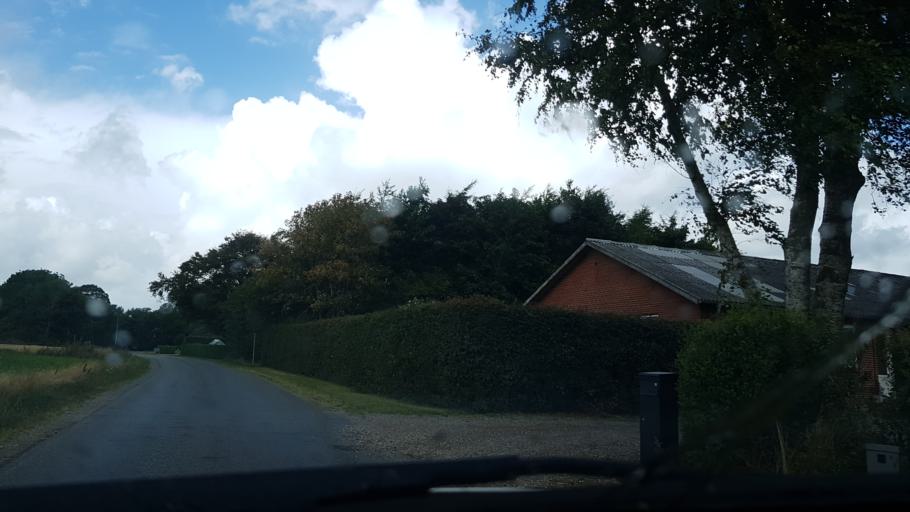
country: DK
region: South Denmark
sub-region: Esbjerg Kommune
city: Ribe
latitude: 55.2453
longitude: 8.8245
